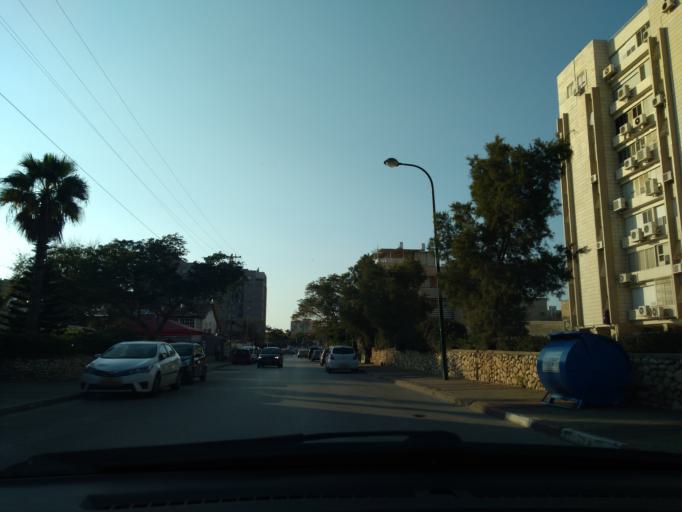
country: IL
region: Central District
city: Even Yehuda
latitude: 32.2821
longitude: 34.8554
